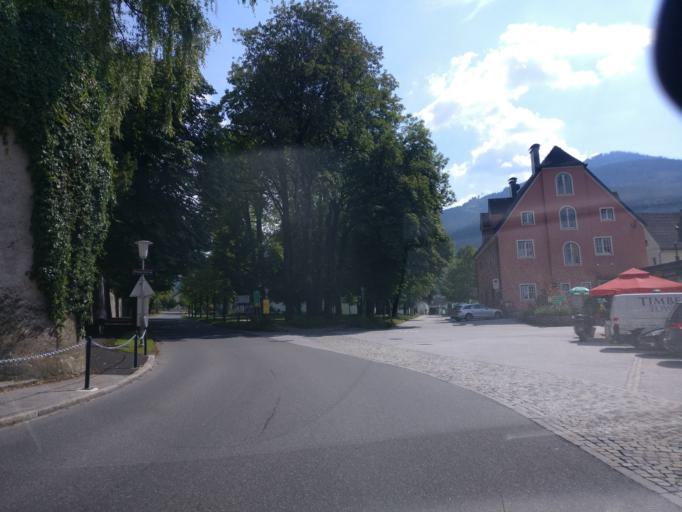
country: AT
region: Styria
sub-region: Politischer Bezirk Liezen
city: Admont
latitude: 47.5753
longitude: 14.4610
